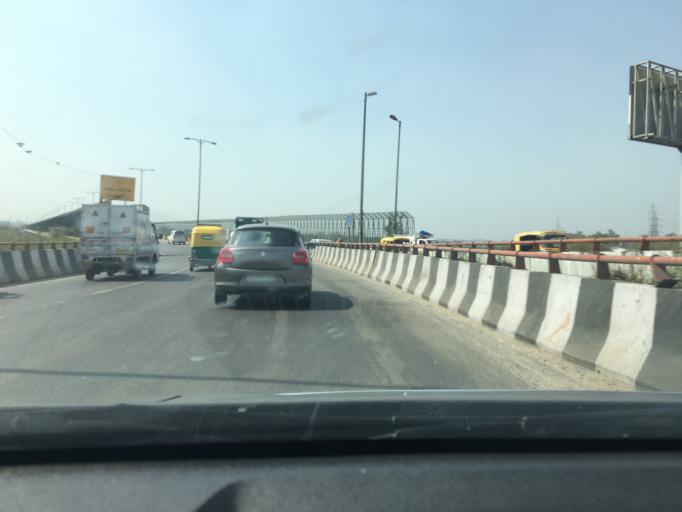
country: IN
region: NCT
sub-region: North Delhi
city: Delhi
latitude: 28.6513
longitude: 77.2664
